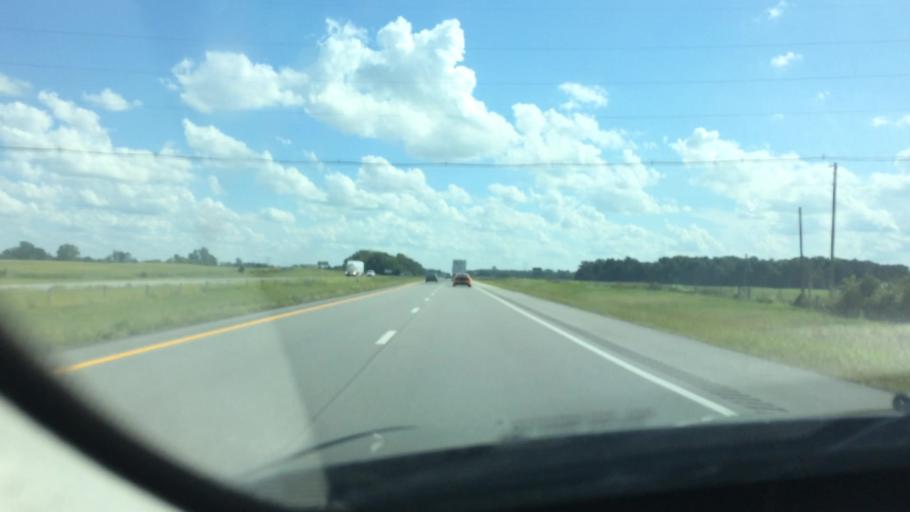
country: US
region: Ohio
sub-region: Auglaize County
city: Wapakoneta
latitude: 40.5484
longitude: -84.1699
